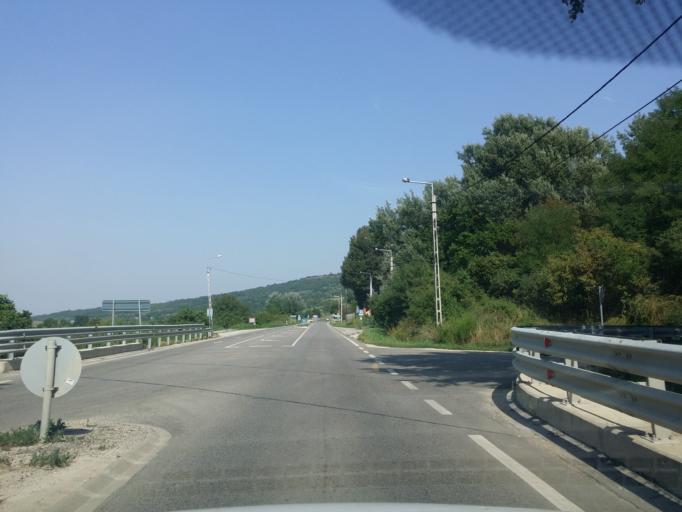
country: HU
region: Tolna
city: Pincehely
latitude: 46.6931
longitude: 18.4566
